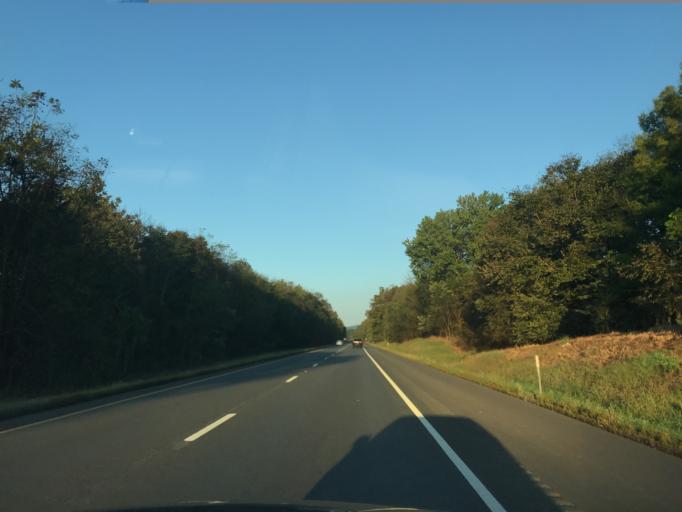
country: US
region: Maryland
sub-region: Washington County
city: Wilson-Conococheague
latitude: 39.6513
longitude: -77.8593
